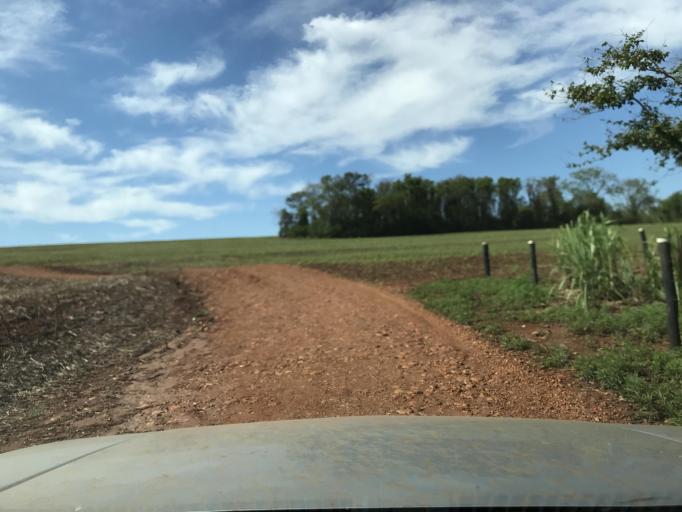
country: BR
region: Parana
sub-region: Palotina
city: Palotina
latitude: -24.1818
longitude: -53.8395
